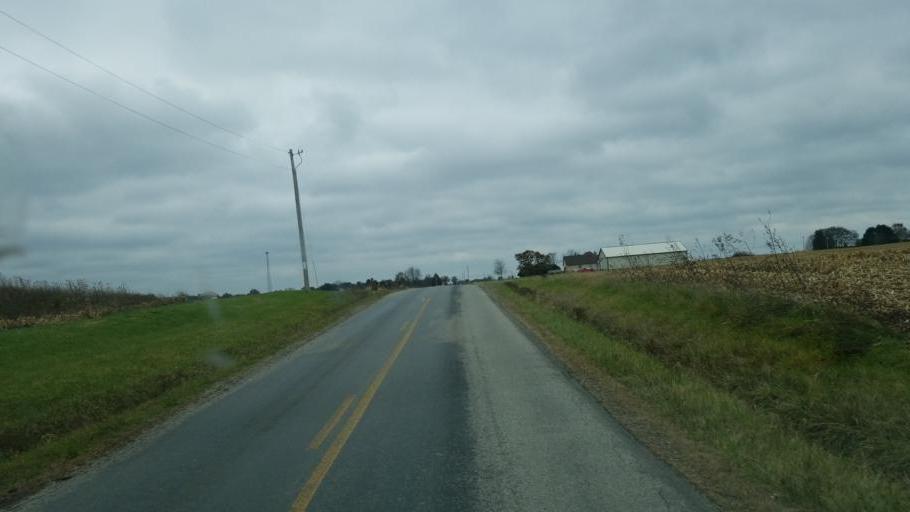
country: US
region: Ohio
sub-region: Licking County
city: Johnstown
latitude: 40.1943
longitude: -82.7569
